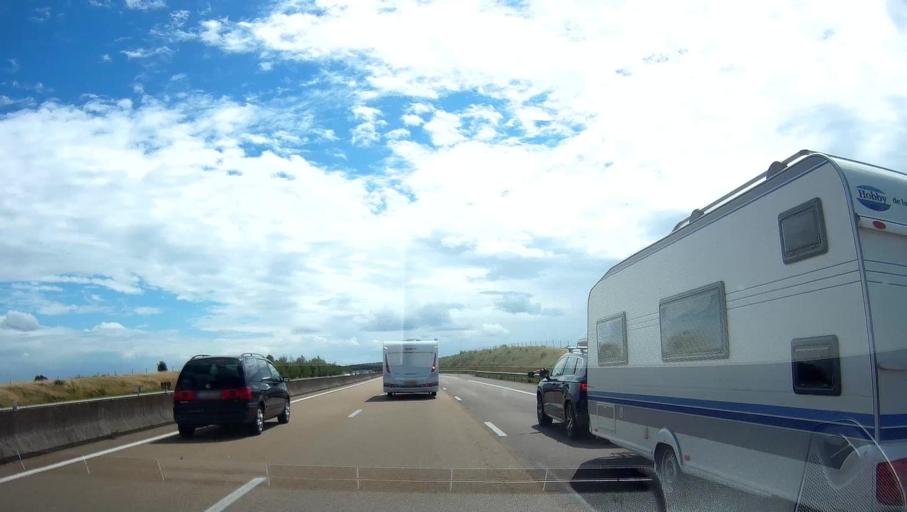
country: FR
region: Bourgogne
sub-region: Departement de la Cote-d'Or
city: Marcilly-sur-Tille
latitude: 47.4918
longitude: 5.1877
